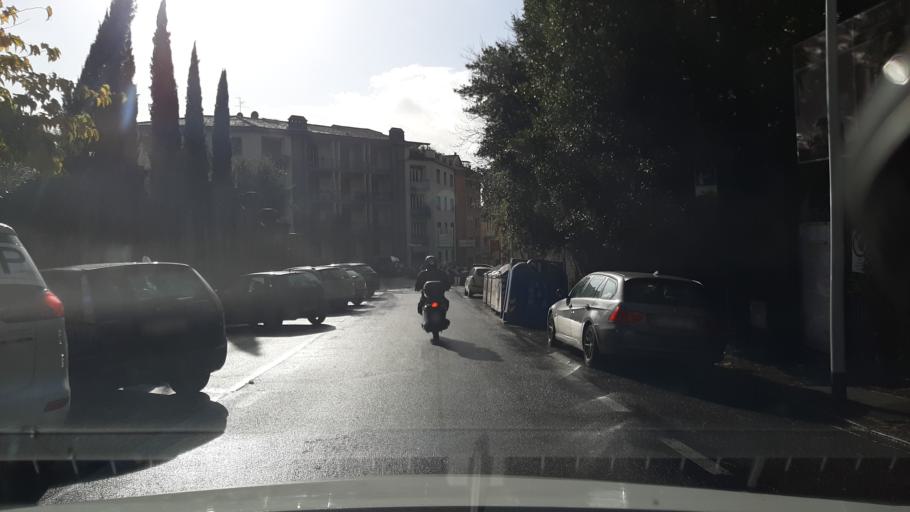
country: IT
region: Tuscany
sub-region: Province of Florence
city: Florence
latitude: 43.7902
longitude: 11.2591
